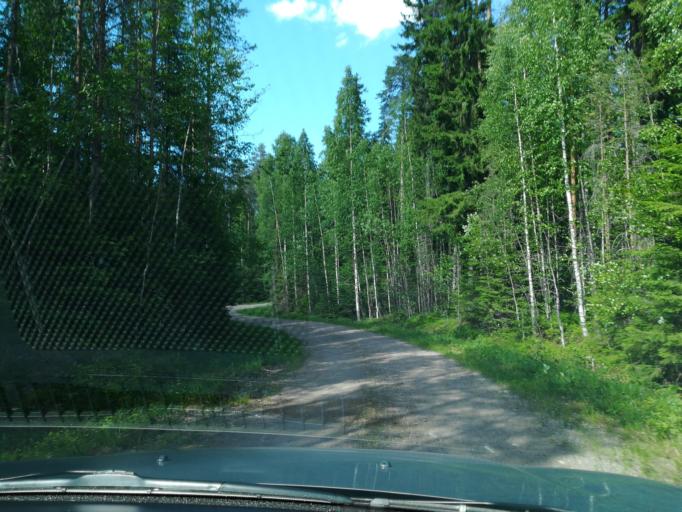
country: FI
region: South Karelia
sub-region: Imatra
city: Ruokolahti
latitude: 61.5490
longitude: 28.8113
